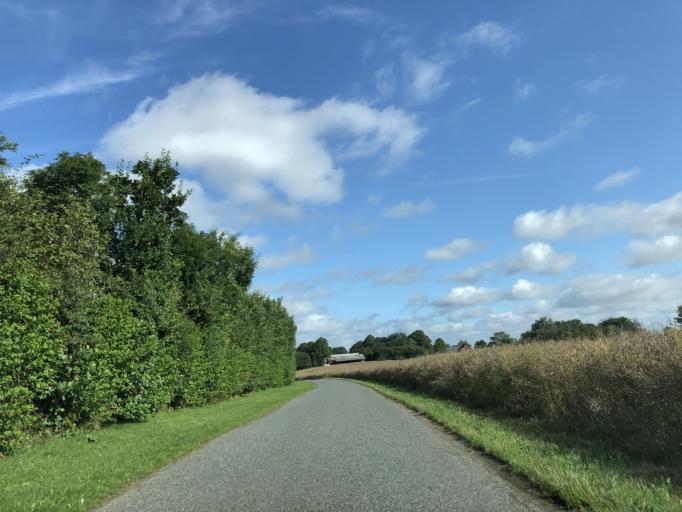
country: DK
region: Central Jutland
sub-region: Silkeborg Kommune
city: Svejbaek
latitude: 56.2228
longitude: 9.6357
